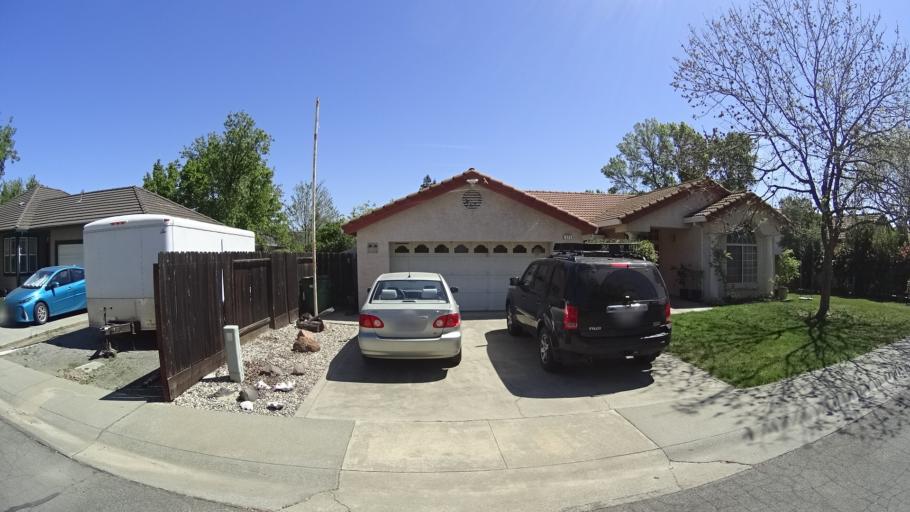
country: US
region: California
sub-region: Glenn County
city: Orland
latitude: 39.7532
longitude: -122.1804
